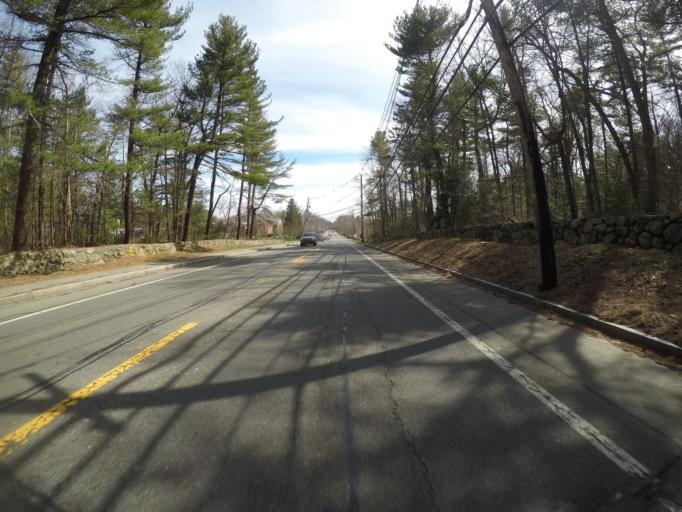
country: US
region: Massachusetts
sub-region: Bristol County
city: Easton
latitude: 42.0635
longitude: -71.0871
